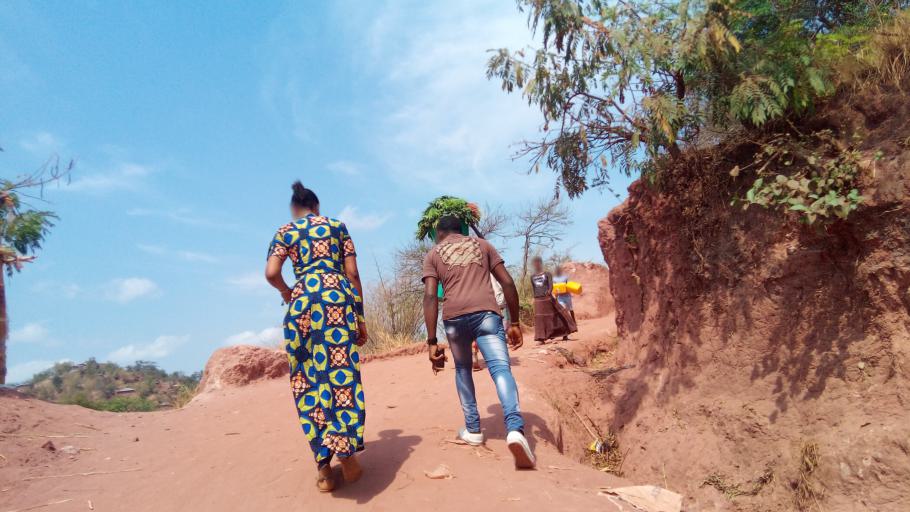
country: CD
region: Katanga
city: Kalemie
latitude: -5.9306
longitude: 29.1913
